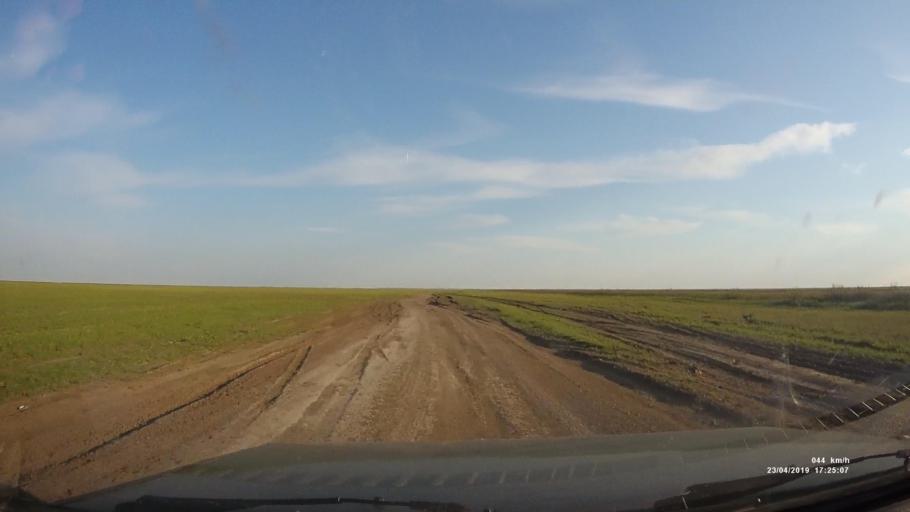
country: RU
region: Kalmykiya
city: Priyutnoye
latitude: 46.1537
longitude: 43.5095
